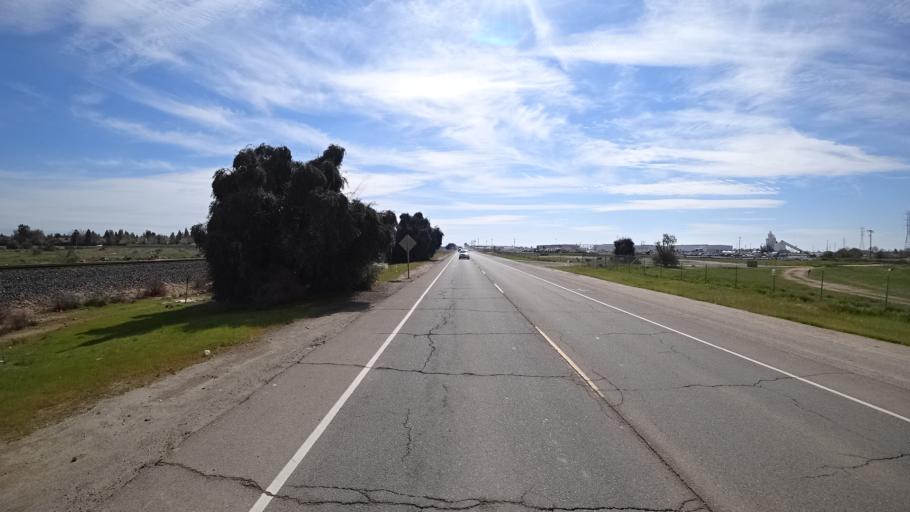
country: US
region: California
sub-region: Fresno County
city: Biola
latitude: 36.8236
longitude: -119.8999
